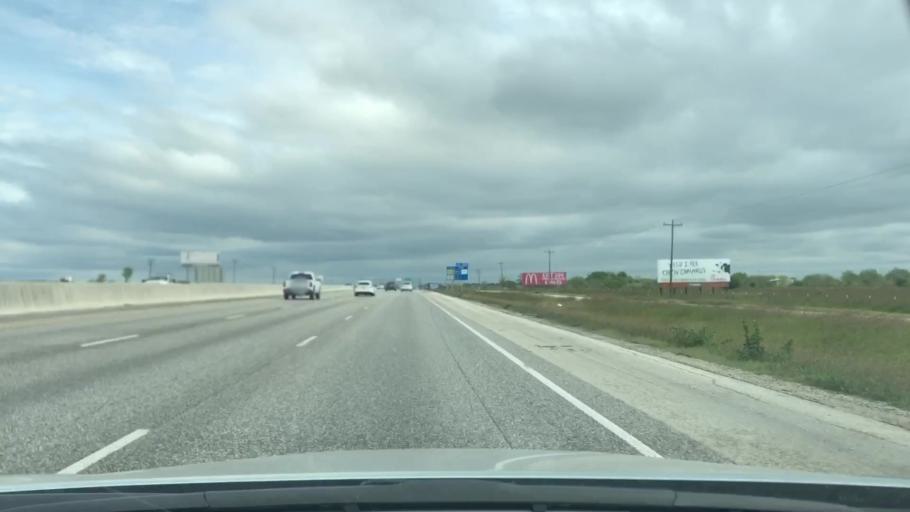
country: US
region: Texas
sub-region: Guadalupe County
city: Redwood
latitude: 29.8023
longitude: -98.0137
